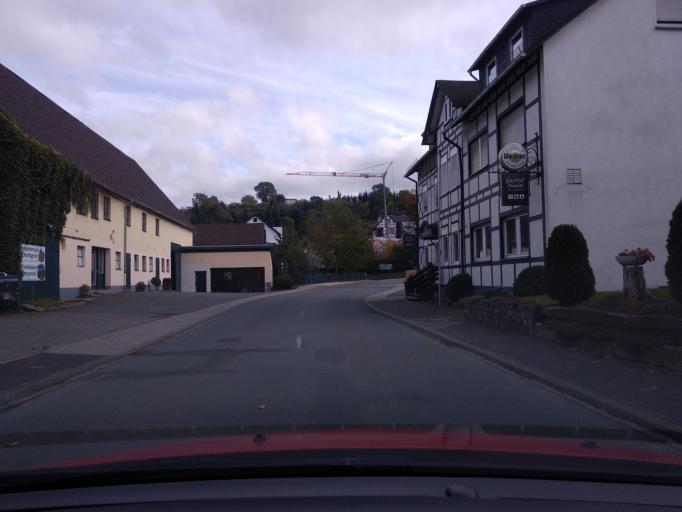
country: DE
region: North Rhine-Westphalia
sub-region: Regierungsbezirk Arnsberg
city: Bestwig
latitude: 51.3332
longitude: 8.4068
